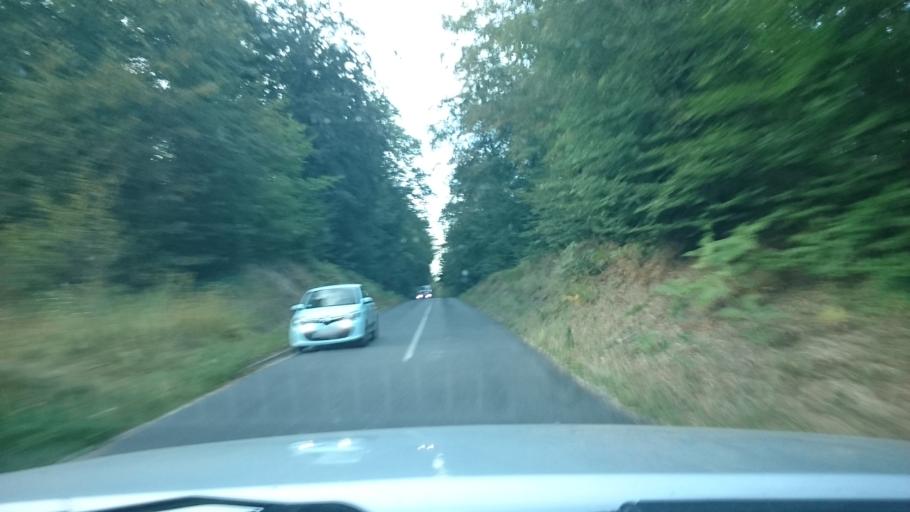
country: FR
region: Ile-de-France
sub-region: Departement de Seine-et-Marne
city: Bois-le-Roi
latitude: 48.4532
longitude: 2.7230
